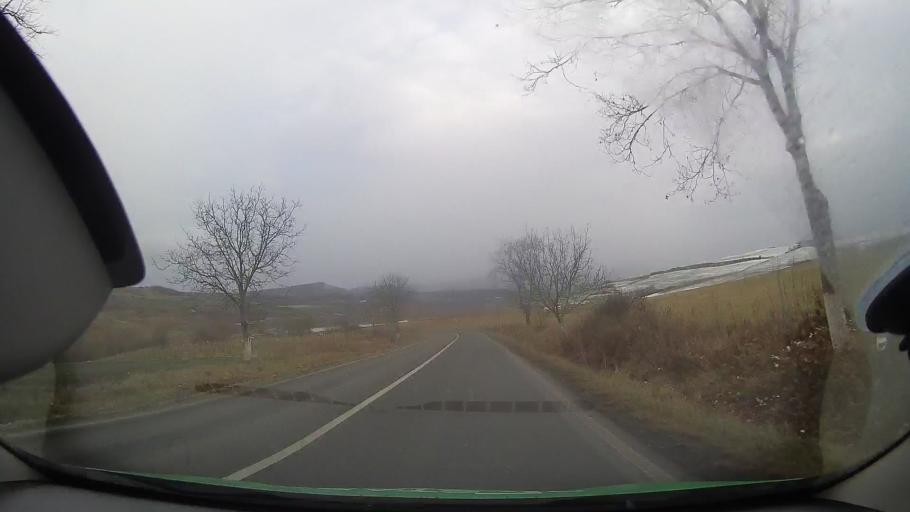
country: RO
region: Sibiu
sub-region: Comuna Blajel
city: Blajel
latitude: 46.2382
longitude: 24.3038
